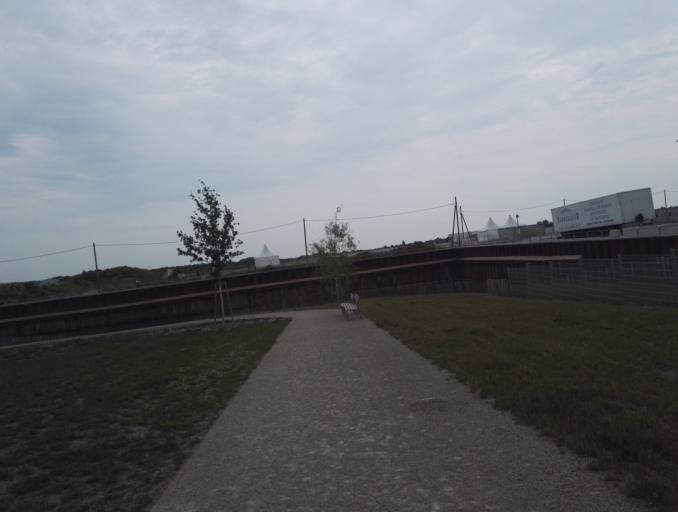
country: AT
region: Lower Austria
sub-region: Politischer Bezirk Ganserndorf
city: Gross-Enzersdorf
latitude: 48.2257
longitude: 16.5098
